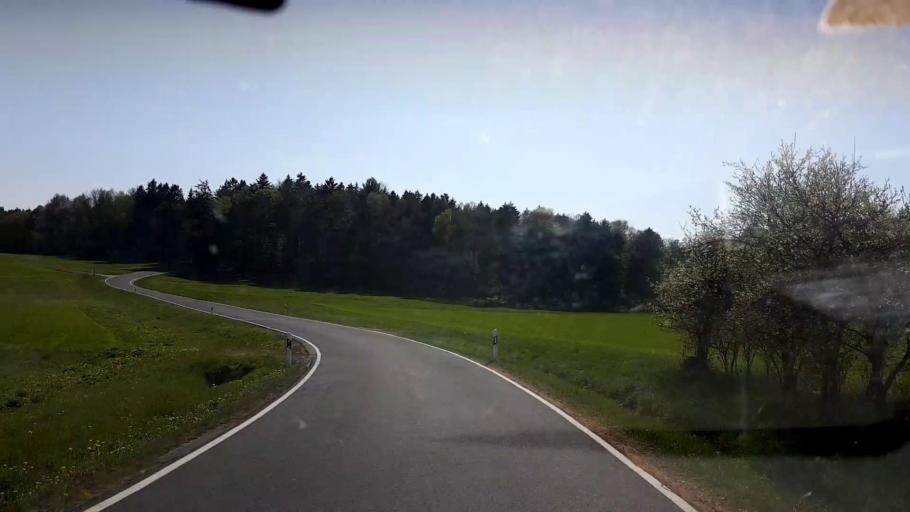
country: DE
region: Bavaria
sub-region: Upper Franconia
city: Pottenstein
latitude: 49.7984
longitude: 11.3991
